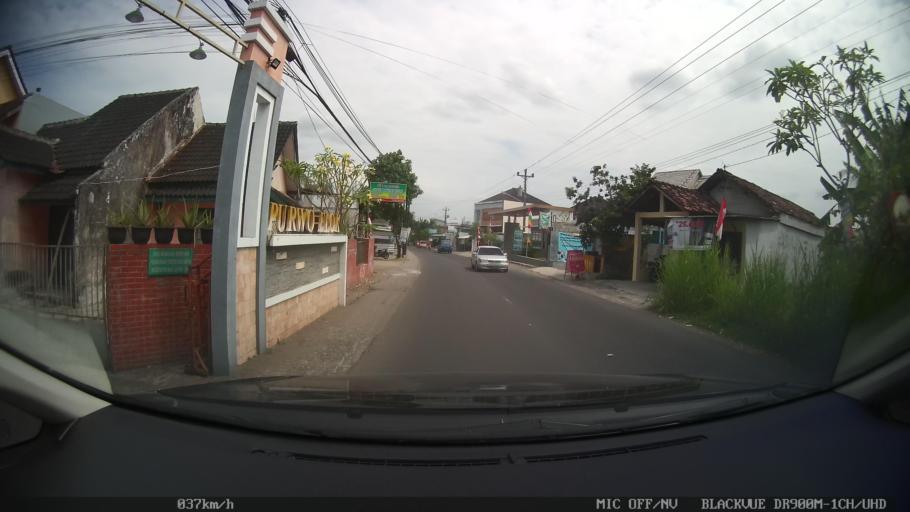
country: ID
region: Daerah Istimewa Yogyakarta
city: Depok
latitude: -7.7401
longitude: 110.4518
